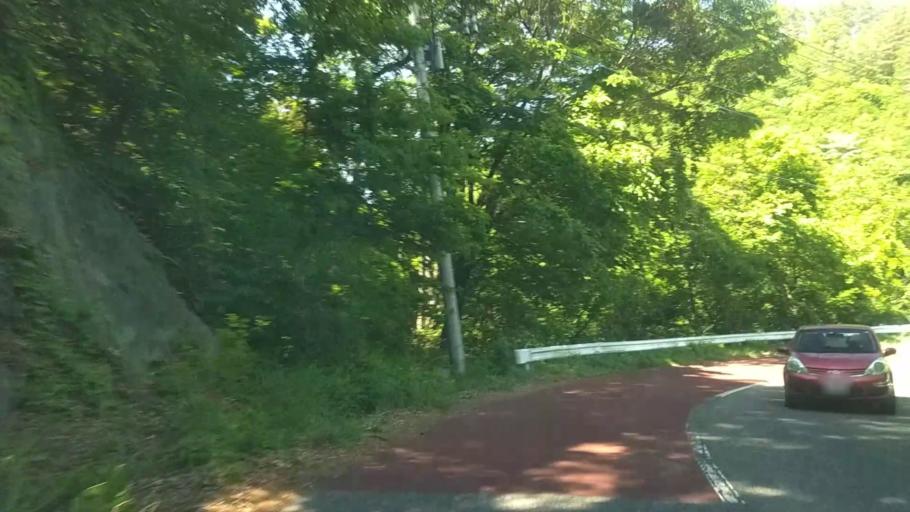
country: JP
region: Yamanashi
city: Nirasaki
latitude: 35.8559
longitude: 138.4324
